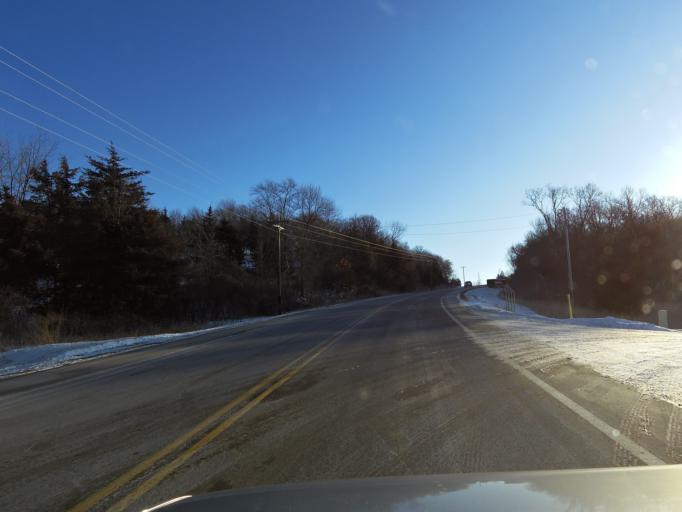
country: US
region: Minnesota
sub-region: Carver County
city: Carver
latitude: 44.7330
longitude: -93.5811
